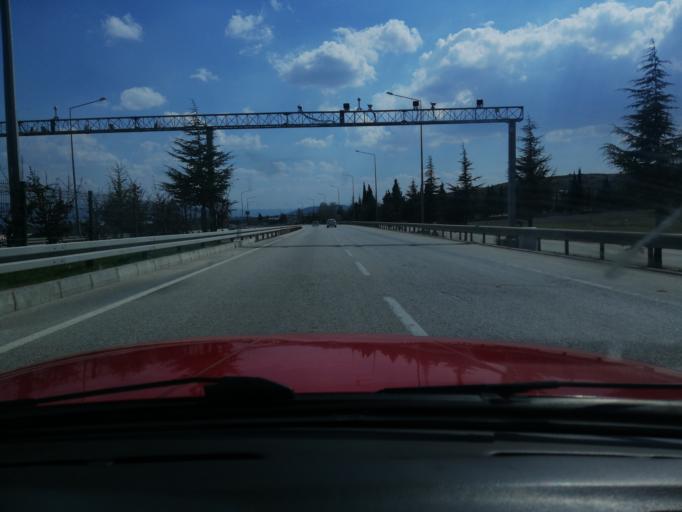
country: TR
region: Isparta
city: Keciborlu
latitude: 37.9252
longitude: 30.3009
